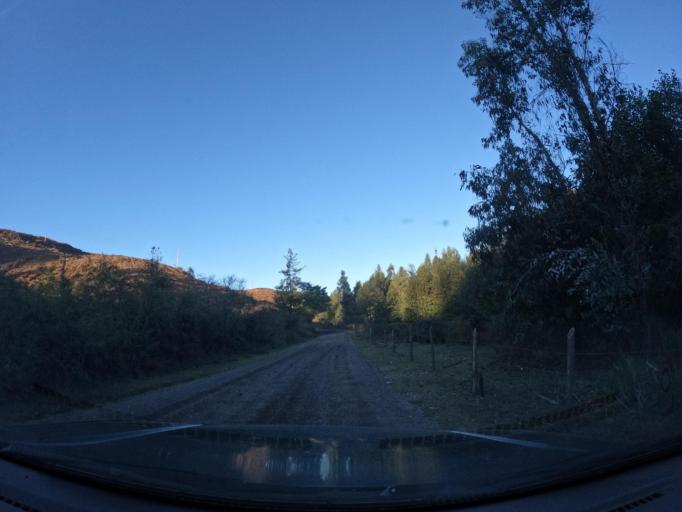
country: CL
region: Biobio
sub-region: Provincia de Concepcion
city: Chiguayante
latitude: -37.0382
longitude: -72.8348
